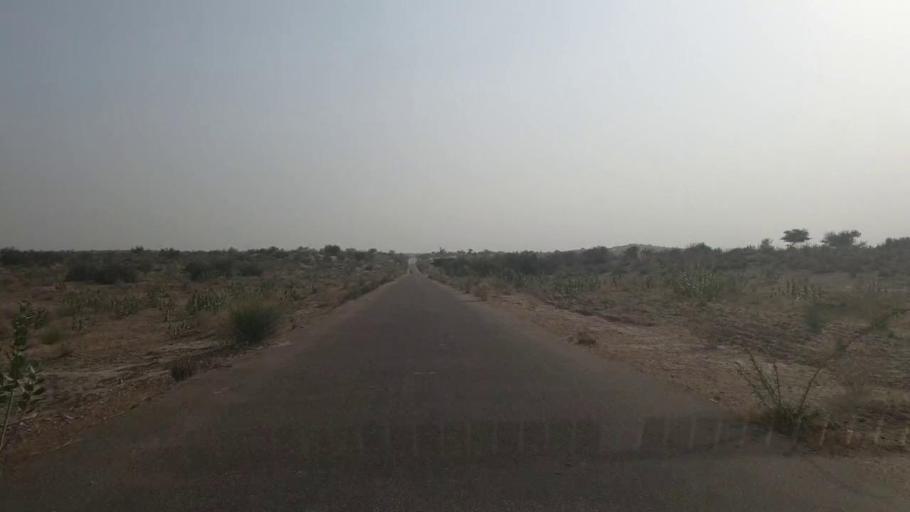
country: PK
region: Sindh
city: Chor
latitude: 25.4646
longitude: 69.9673
